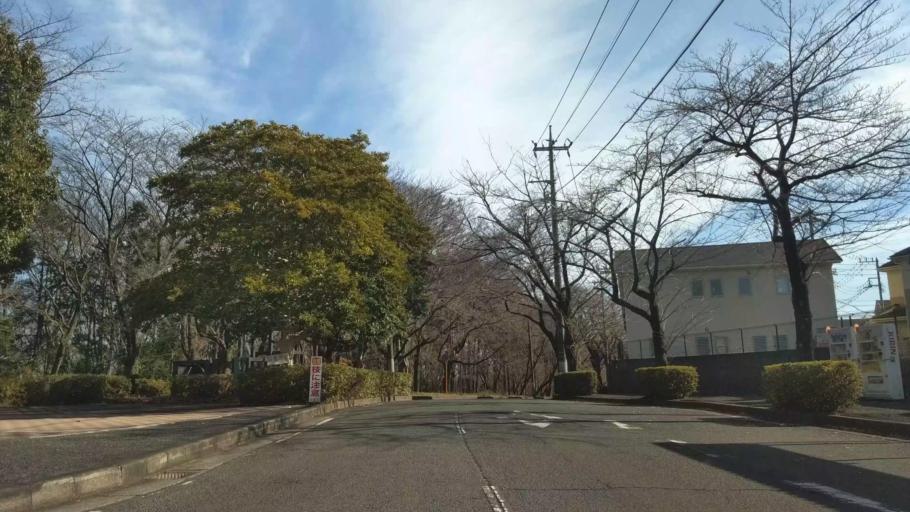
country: JP
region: Kanagawa
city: Hadano
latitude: 35.3588
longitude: 139.2255
